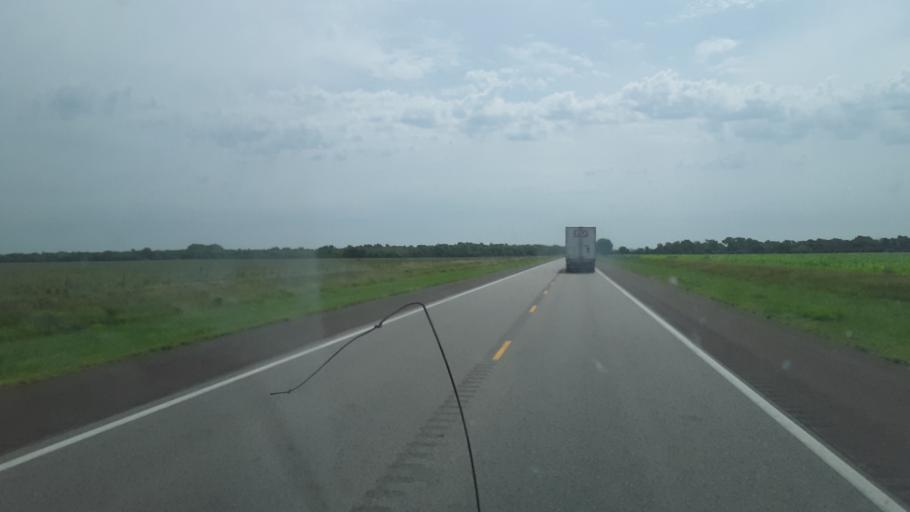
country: US
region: Kansas
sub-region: Reno County
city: Nickerson
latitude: 37.9850
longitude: -98.1507
